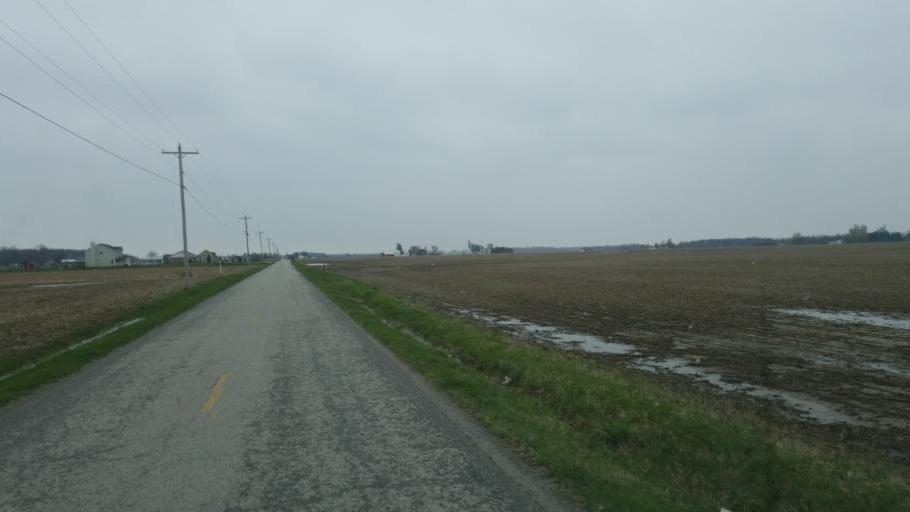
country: US
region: Ohio
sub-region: Marion County
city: Prospect
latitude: 40.3972
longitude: -83.1174
